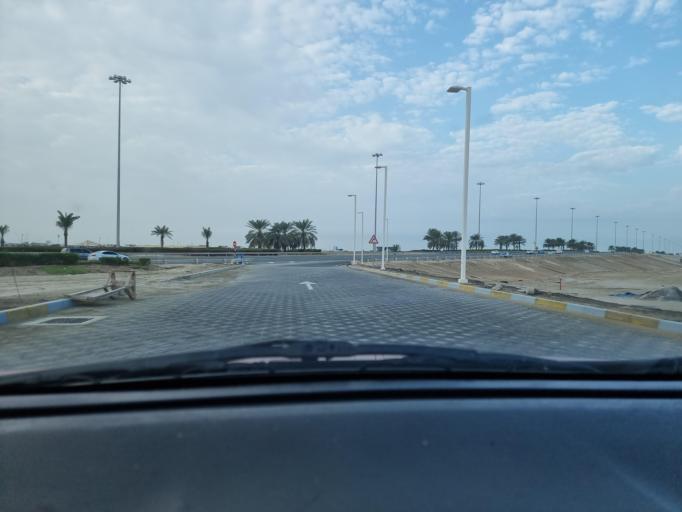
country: AE
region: Abu Dhabi
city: Abu Dhabi
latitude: 24.5016
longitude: 54.5874
